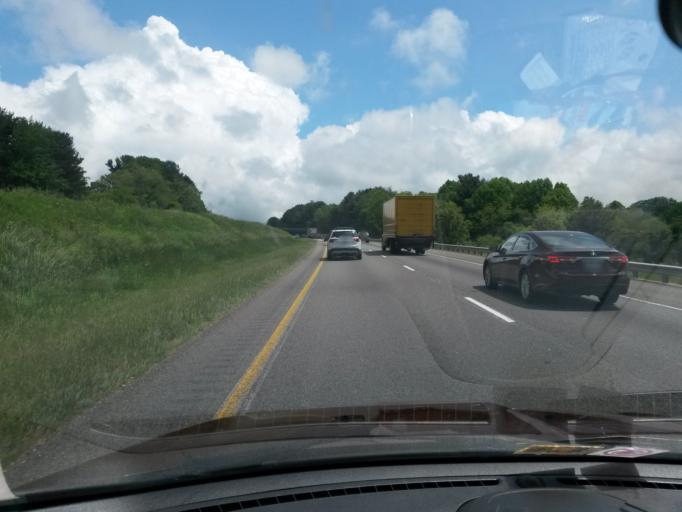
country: US
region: Virginia
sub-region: Carroll County
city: Hillsville
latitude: 36.6985
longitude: -80.7383
